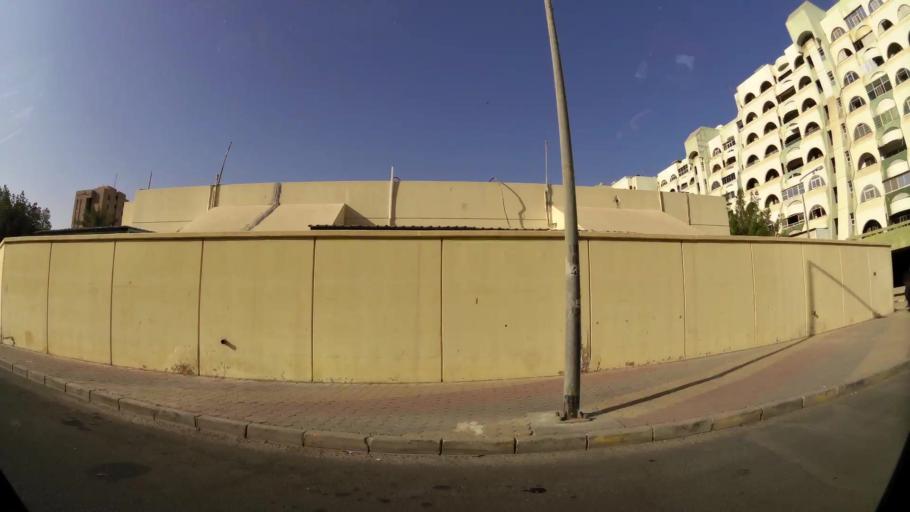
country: KW
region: Al Asimah
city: Kuwait City
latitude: 29.3758
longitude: 47.9850
